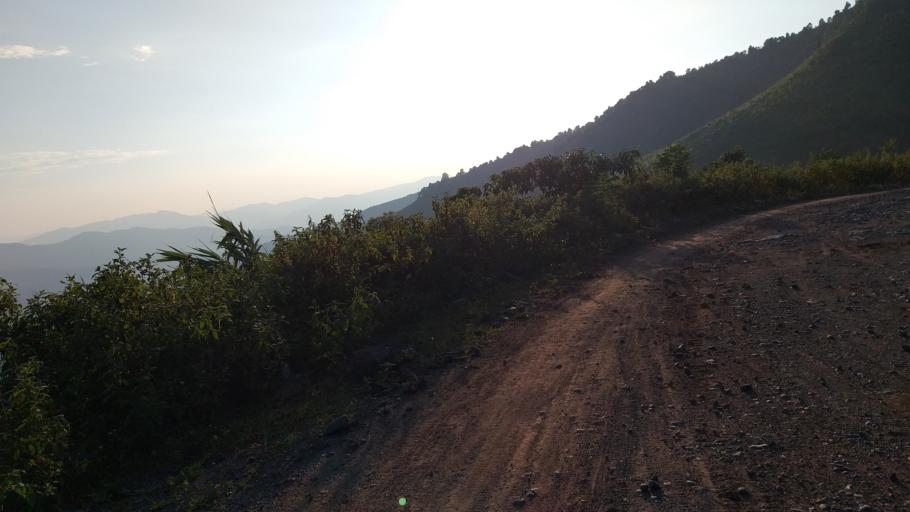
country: LA
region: Phongsali
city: Khoa
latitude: 21.2042
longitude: 102.5882
